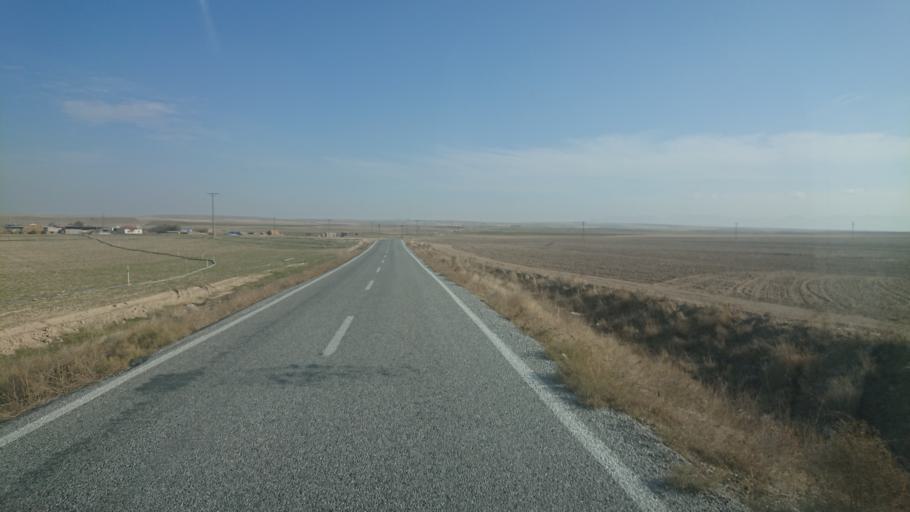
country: TR
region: Aksaray
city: Sultanhani
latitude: 38.0372
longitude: 33.6010
